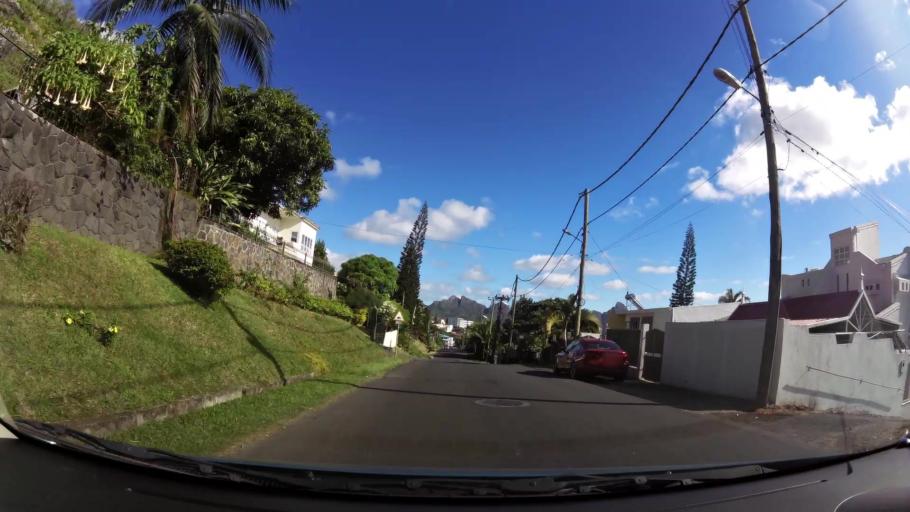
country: MU
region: Plaines Wilhems
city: Quatre Bornes
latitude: -20.2738
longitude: 57.4812
